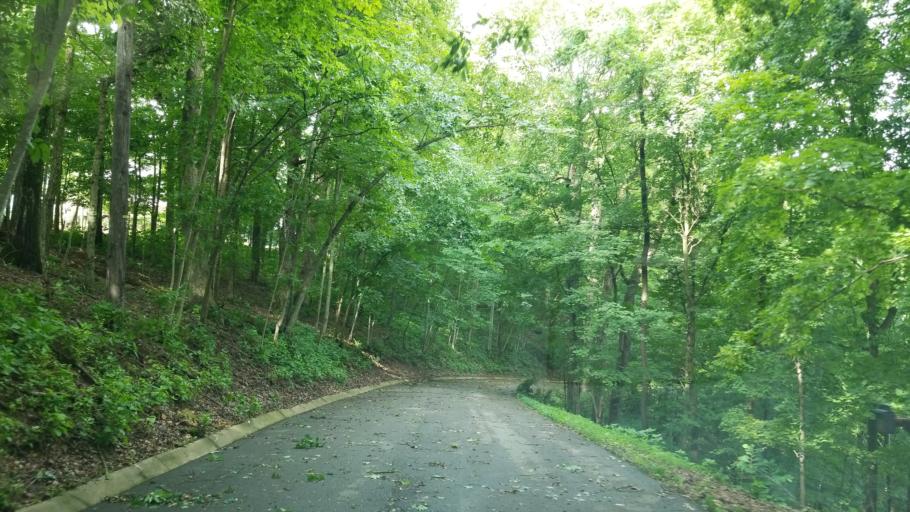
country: US
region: Tennessee
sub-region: Williamson County
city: Brentwood
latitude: 36.0533
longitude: -86.8045
